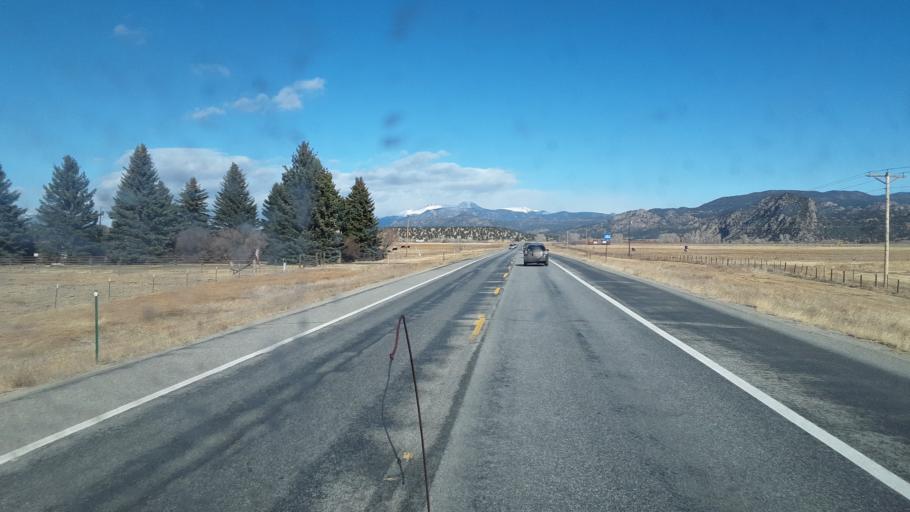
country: US
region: Colorado
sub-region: Chaffee County
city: Buena Vista
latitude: 38.7295
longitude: -106.0859
